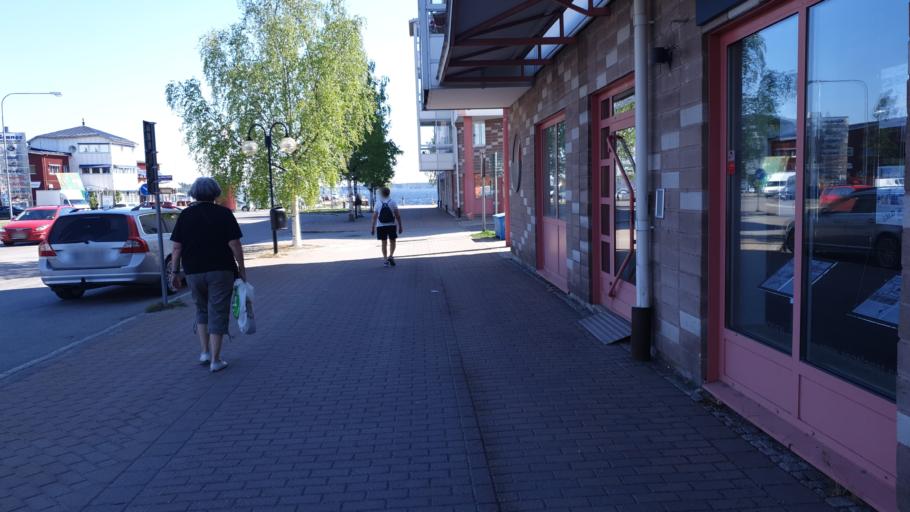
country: SE
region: Norrbotten
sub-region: Lulea Kommun
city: Lulea
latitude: 65.5812
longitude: 22.1589
